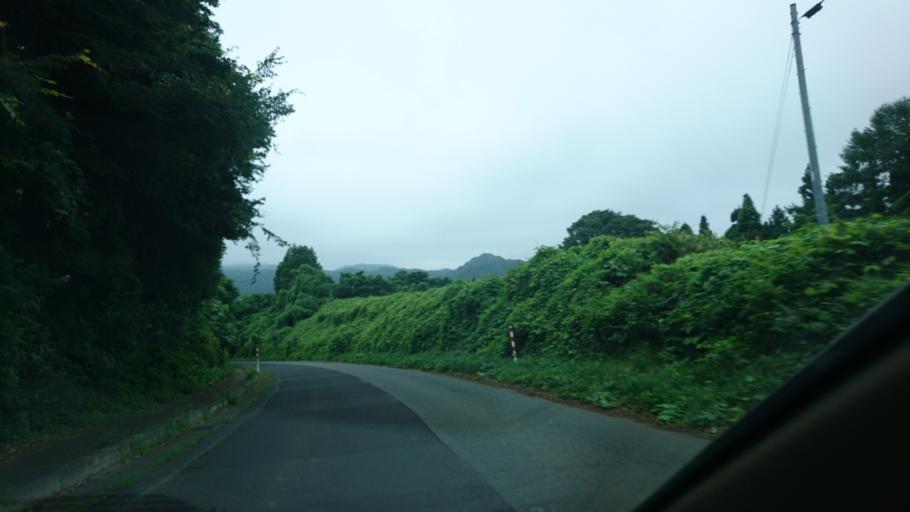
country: JP
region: Iwate
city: Kitakami
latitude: 39.2651
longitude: 141.1116
